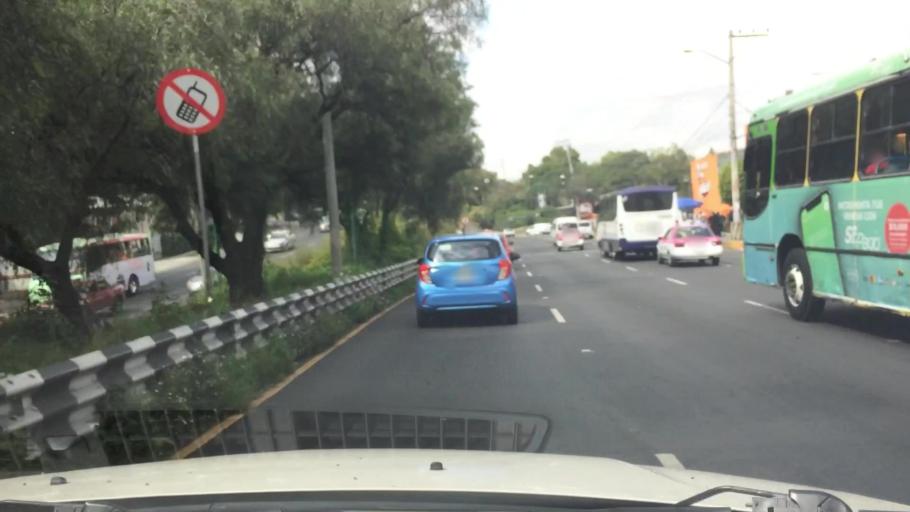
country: MX
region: Mexico City
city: Magdalena Contreras
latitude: 19.2987
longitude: -99.2111
